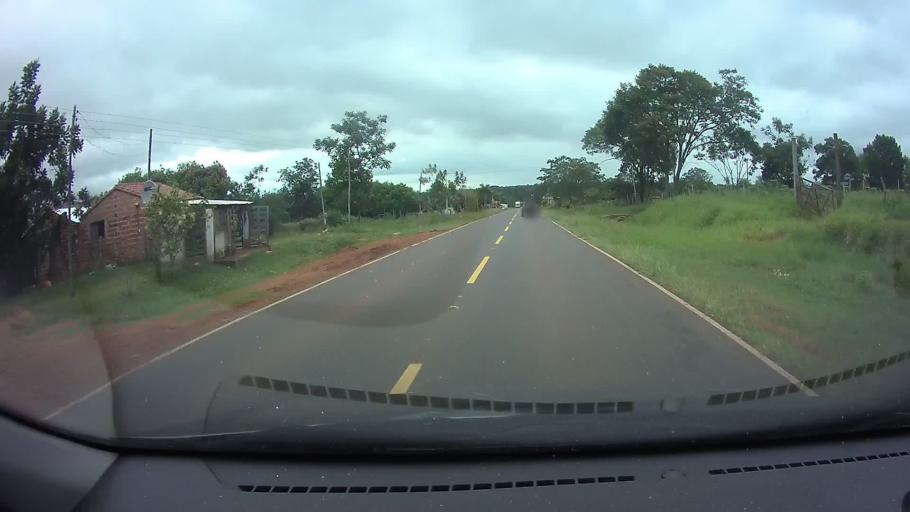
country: PY
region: Paraguari
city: Carapegua
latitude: -25.7330
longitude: -57.3035
